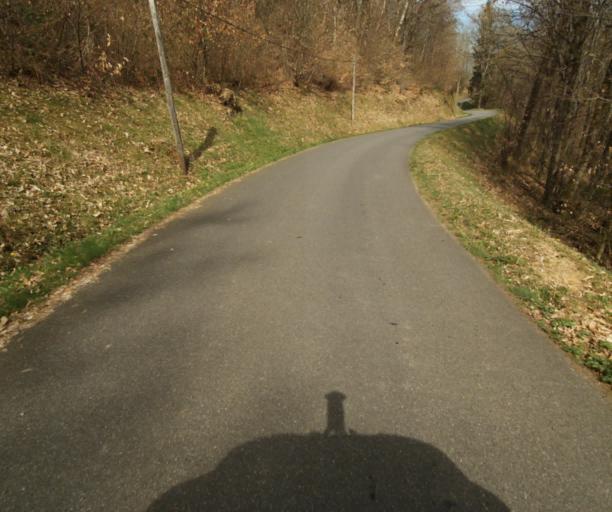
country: FR
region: Limousin
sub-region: Departement de la Correze
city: Naves
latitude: 45.3333
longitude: 1.8023
